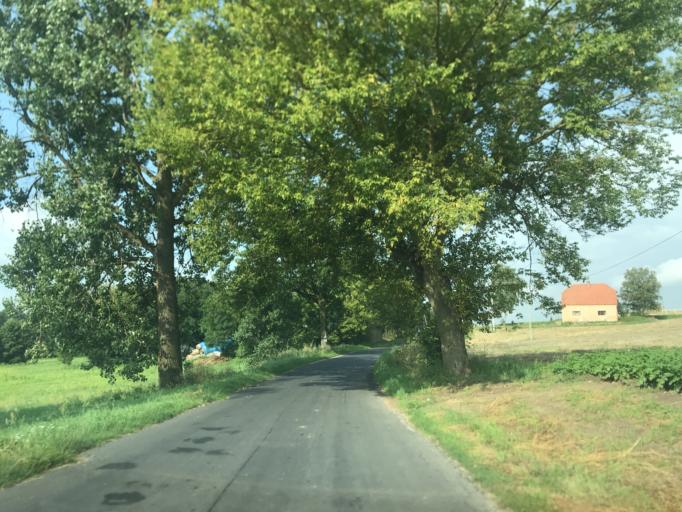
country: PL
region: Warmian-Masurian Voivodeship
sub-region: Powiat nowomiejski
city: Kurzetnik
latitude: 53.3691
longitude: 19.5766
